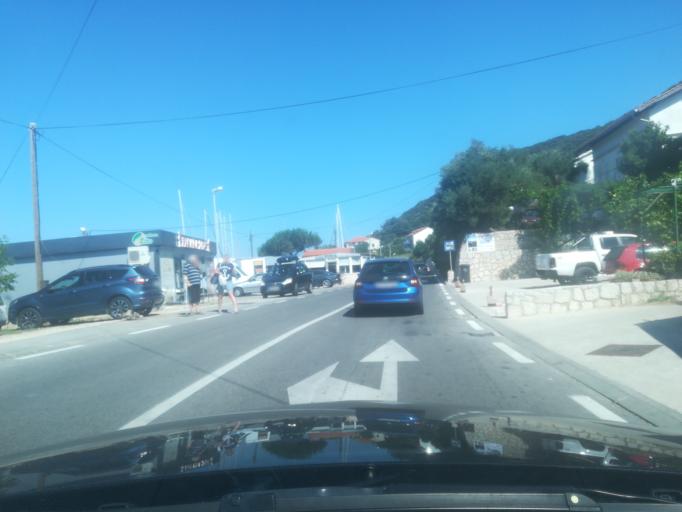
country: HR
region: Primorsko-Goranska
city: Supetarska Draga
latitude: 44.8035
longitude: 14.7264
